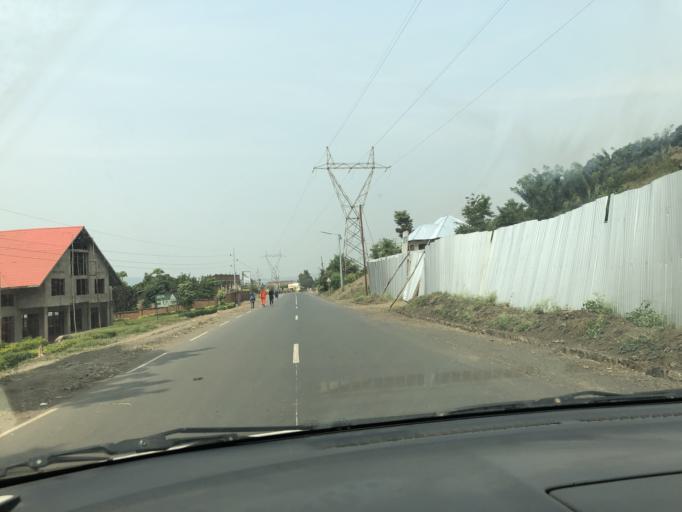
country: BI
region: Cibitoke
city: Cibitoke
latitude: -2.6978
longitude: 29.0048
